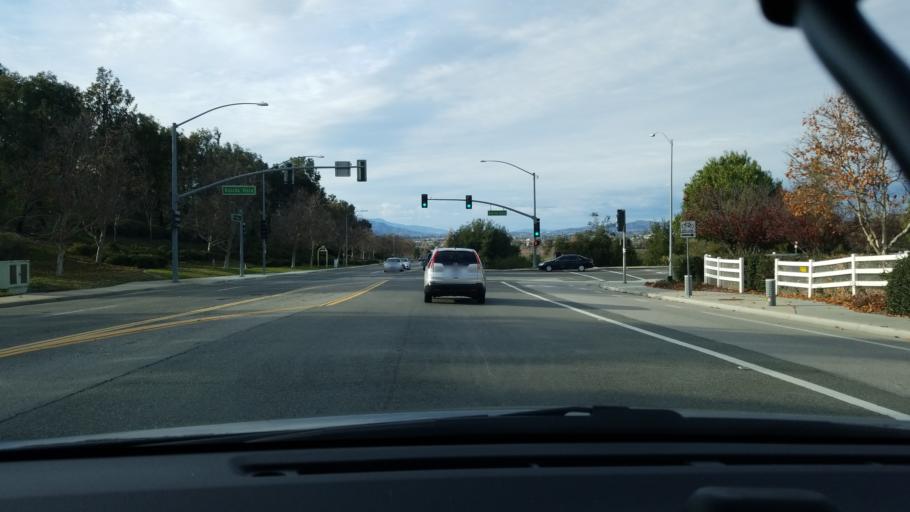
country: US
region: California
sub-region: Riverside County
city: Temecula
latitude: 33.4979
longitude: -117.1419
